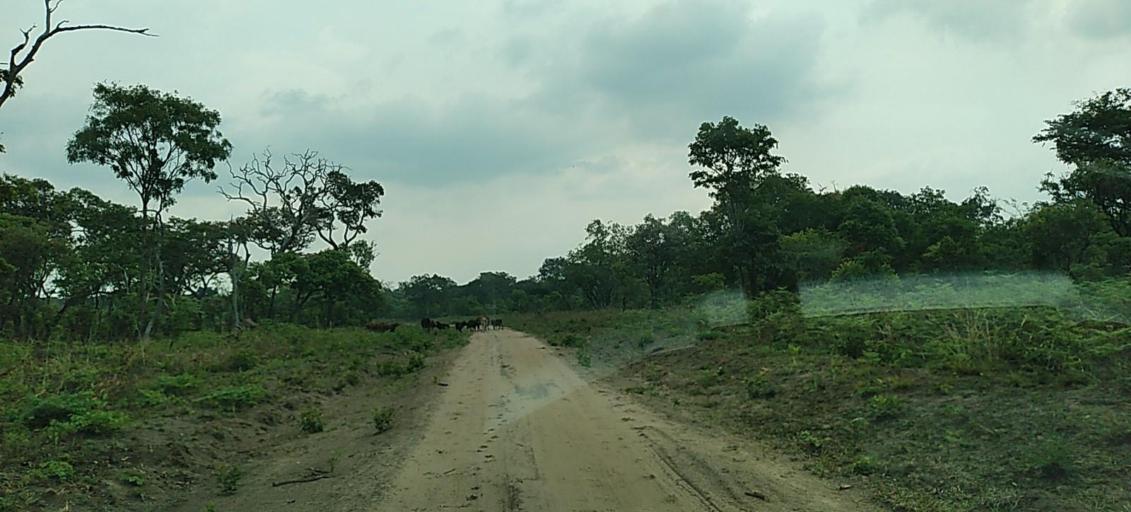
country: ZM
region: North-Western
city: Mwinilunga
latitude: -11.4074
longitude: 24.6229
